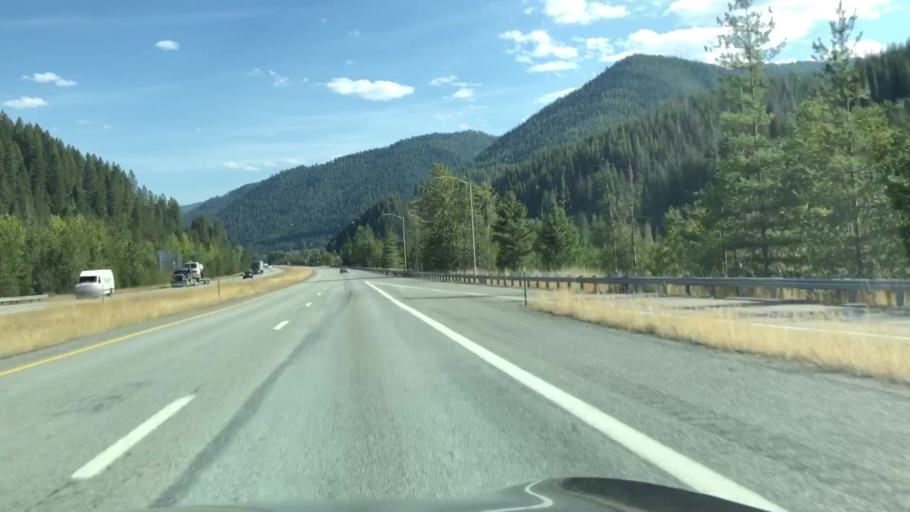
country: US
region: Idaho
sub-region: Shoshone County
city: Osburn
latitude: 47.5256
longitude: -116.0466
